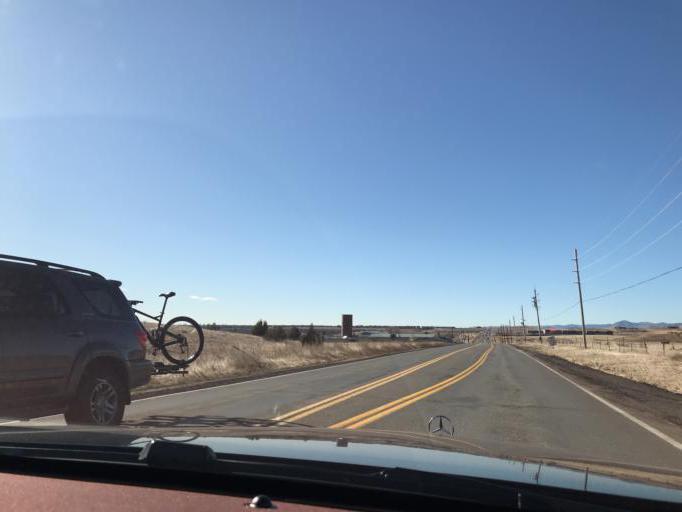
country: US
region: Colorado
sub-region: Boulder County
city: Superior
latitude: 39.8745
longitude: -105.1655
